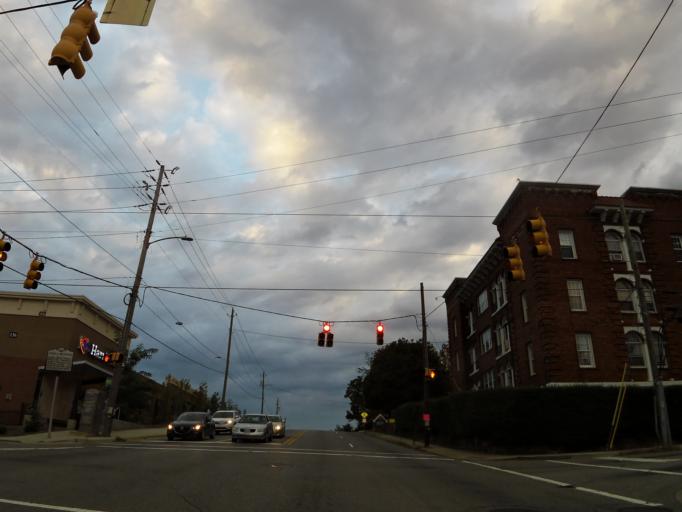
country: US
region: North Carolina
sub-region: Buncombe County
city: Asheville
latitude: 35.6032
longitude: -82.5532
